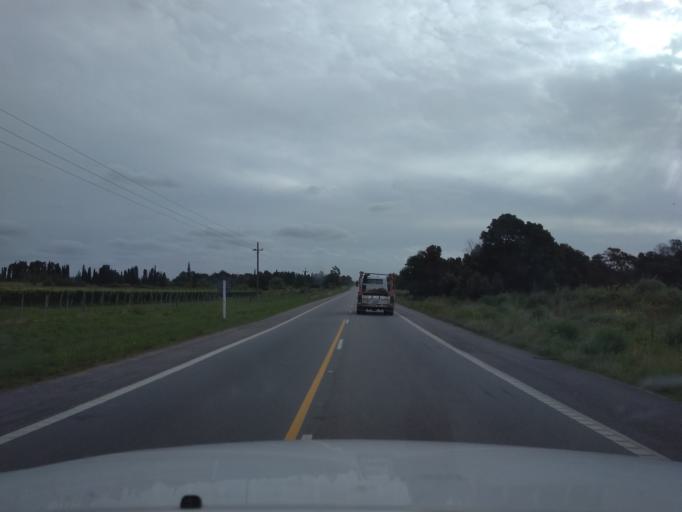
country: UY
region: Canelones
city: Joaquin Suarez
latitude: -34.6832
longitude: -56.0195
